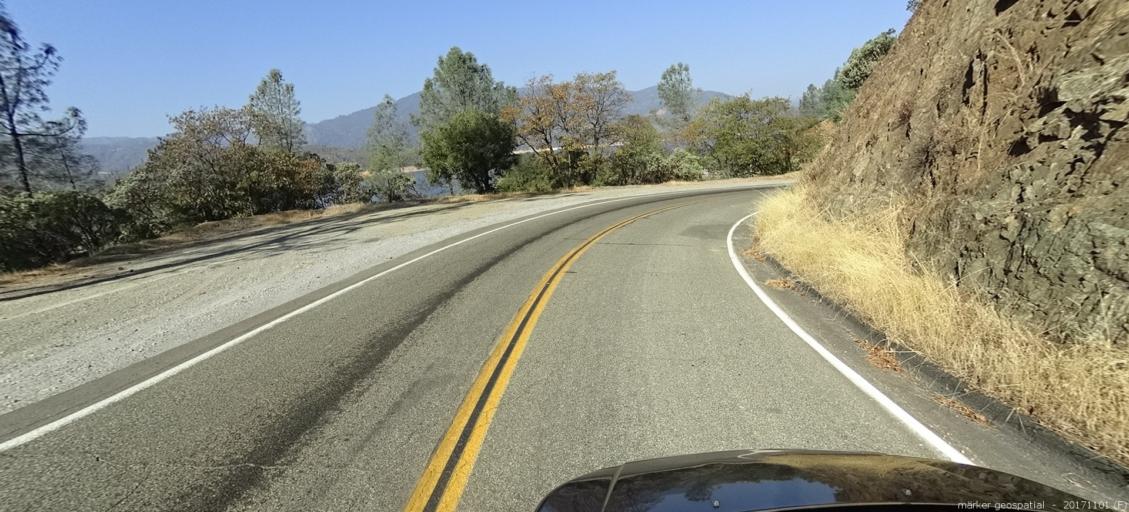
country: US
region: California
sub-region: Shasta County
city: Central Valley (historical)
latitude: 40.7153
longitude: -122.4051
